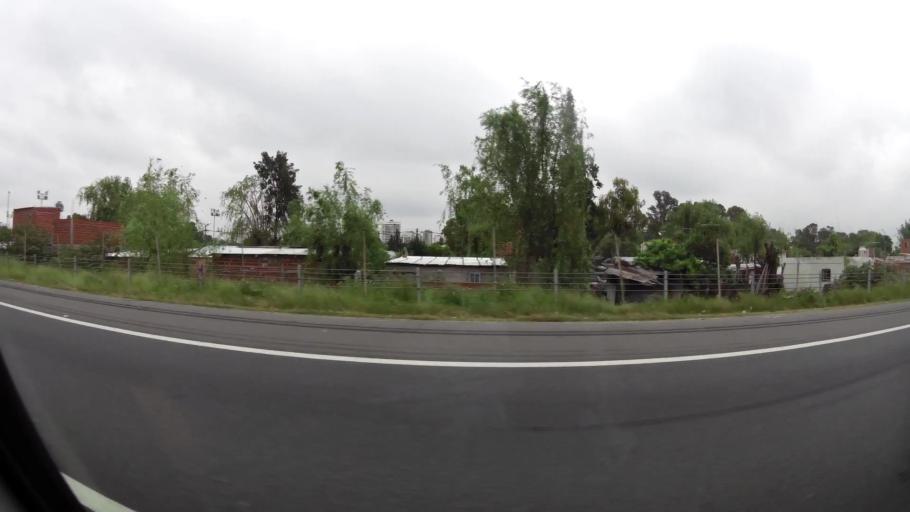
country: AR
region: Buenos Aires
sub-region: Partido de Quilmes
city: Quilmes
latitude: -34.7116
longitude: -58.2522
